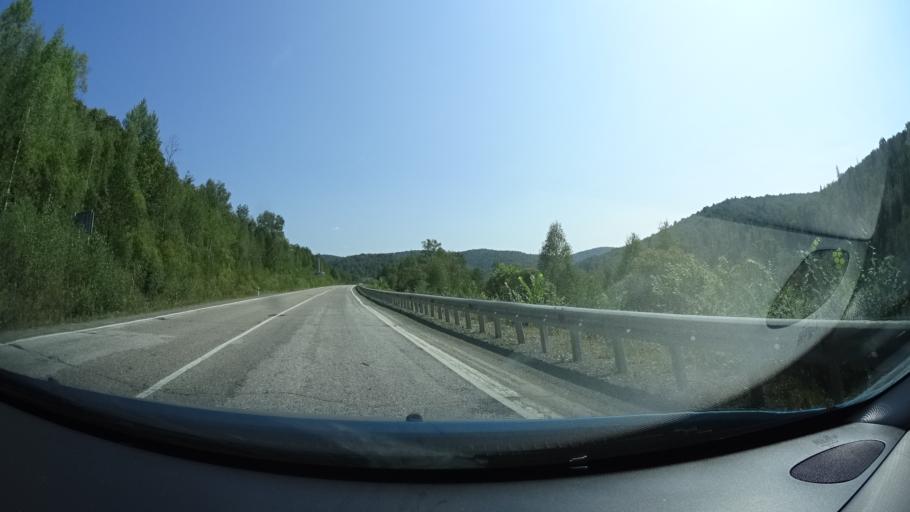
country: RU
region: Bashkortostan
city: Inzer
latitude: 54.3382
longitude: 57.1488
